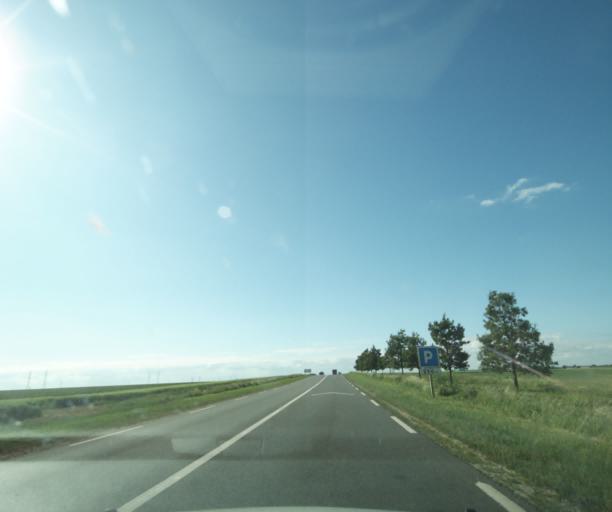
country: FR
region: Centre
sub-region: Departement d'Eure-et-Loir
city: Janville
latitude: 48.2104
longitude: 1.8173
